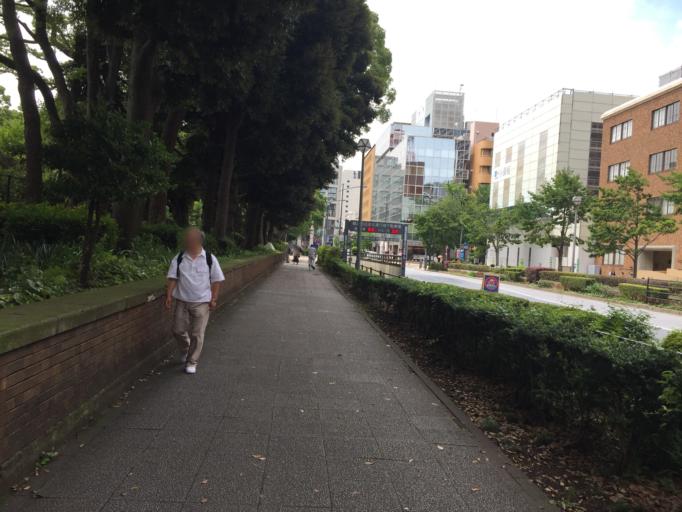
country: JP
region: Kanagawa
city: Yokohama
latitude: 35.4444
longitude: 139.6420
